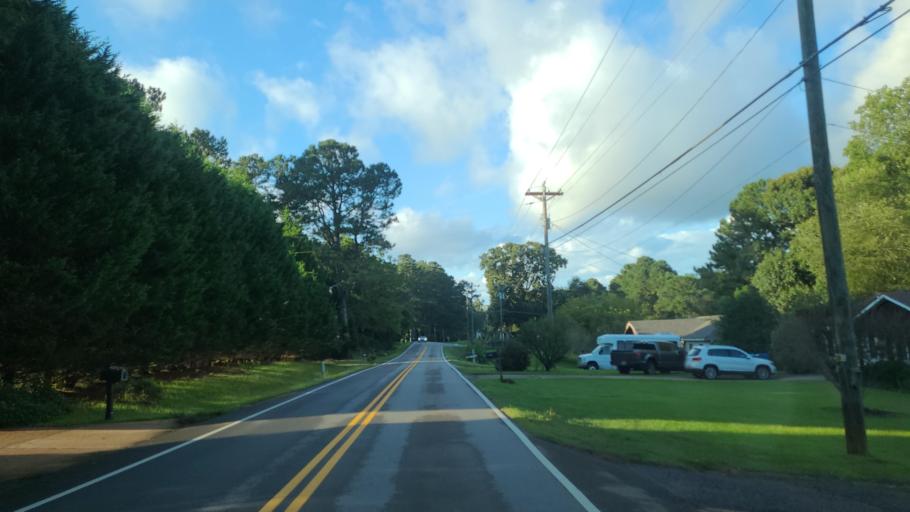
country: US
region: Georgia
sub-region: Fulton County
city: Milton
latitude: 34.1945
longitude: -84.2714
